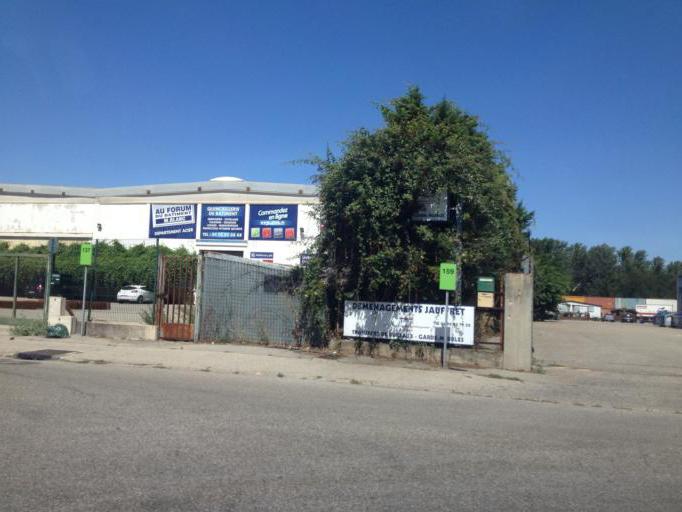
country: FR
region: Provence-Alpes-Cote d'Azur
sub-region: Departement du Vaucluse
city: Avignon
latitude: 43.9346
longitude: 4.7841
